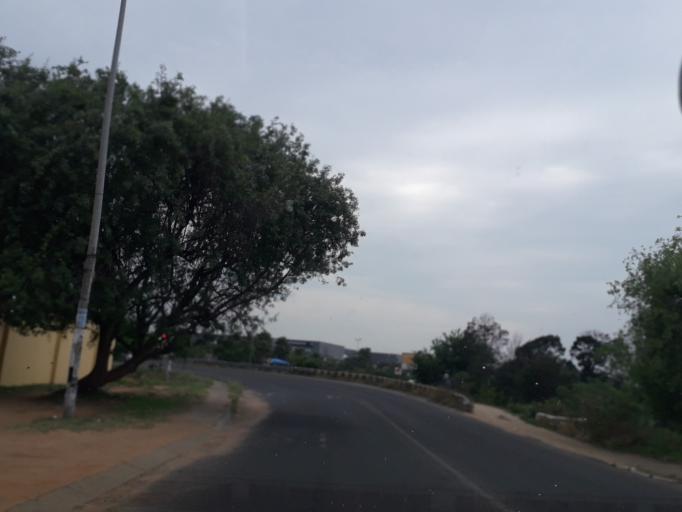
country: ZA
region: Gauteng
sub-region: West Rand District Municipality
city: Muldersdriseloop
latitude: -26.0654
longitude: 27.9440
